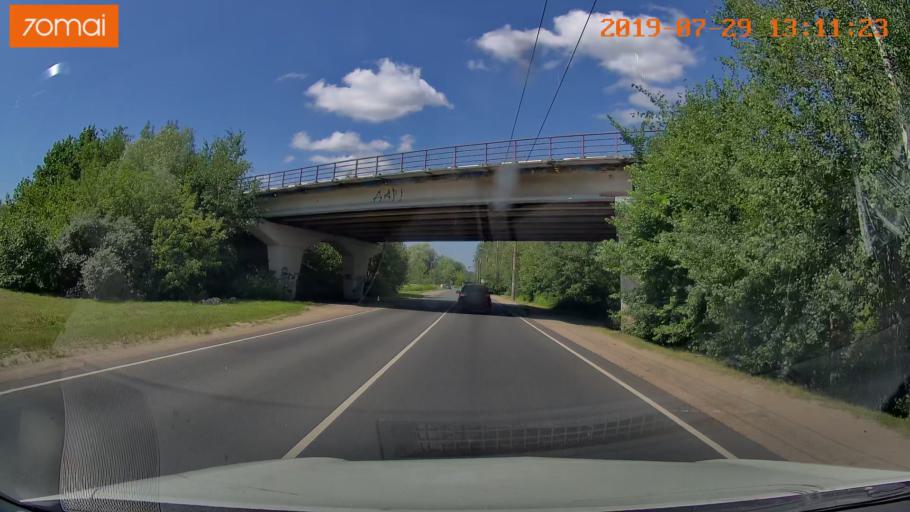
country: RU
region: Kaliningrad
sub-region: Gorod Kaliningrad
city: Kaliningrad
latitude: 54.7194
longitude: 20.3876
